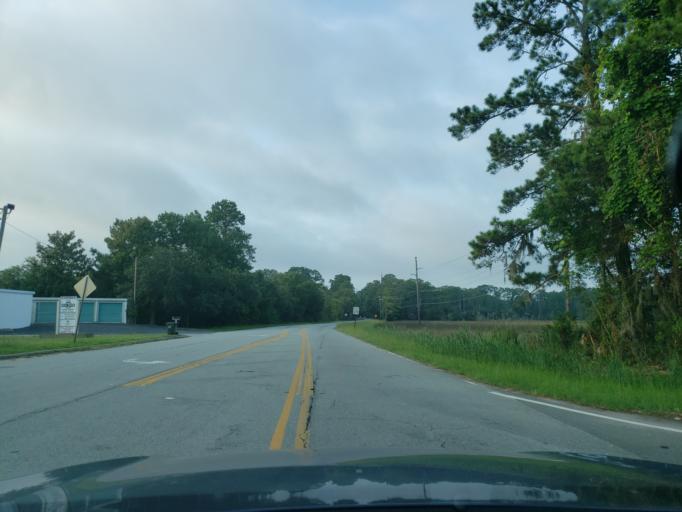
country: US
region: Georgia
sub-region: Chatham County
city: Wilmington Island
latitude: 32.0309
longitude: -80.9723
